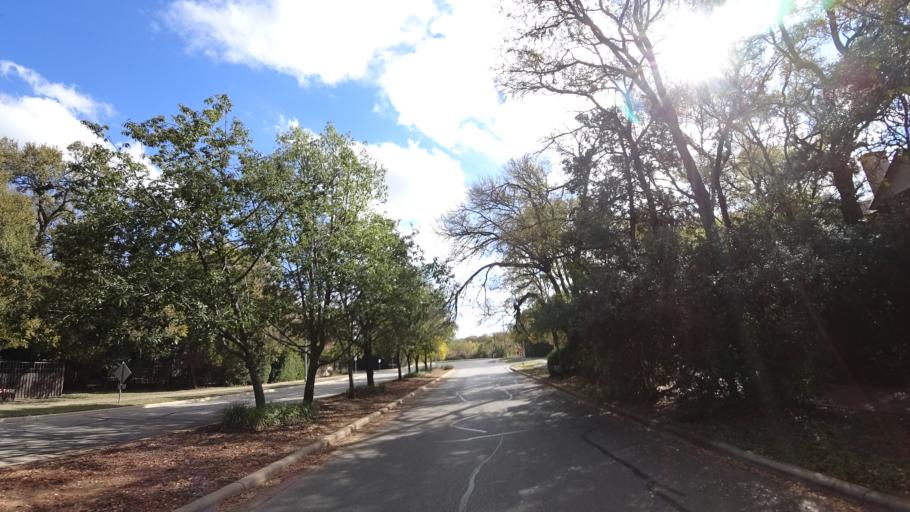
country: US
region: Texas
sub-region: Williamson County
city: Jollyville
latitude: 30.4299
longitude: -97.7419
